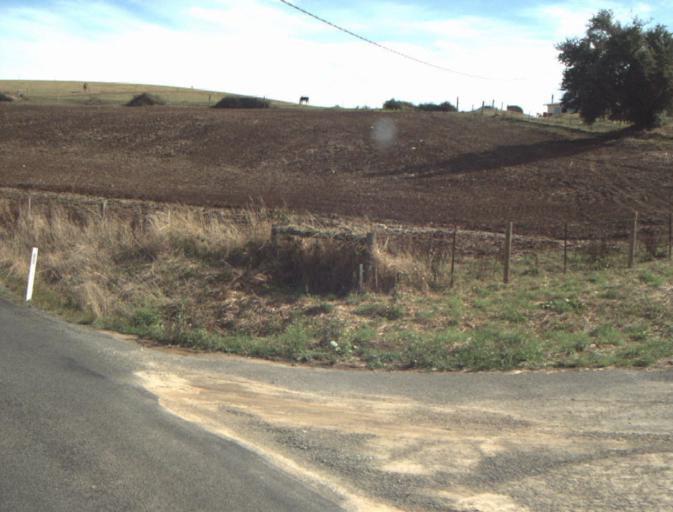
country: AU
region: Tasmania
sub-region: Launceston
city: Mayfield
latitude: -41.1820
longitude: 147.2230
